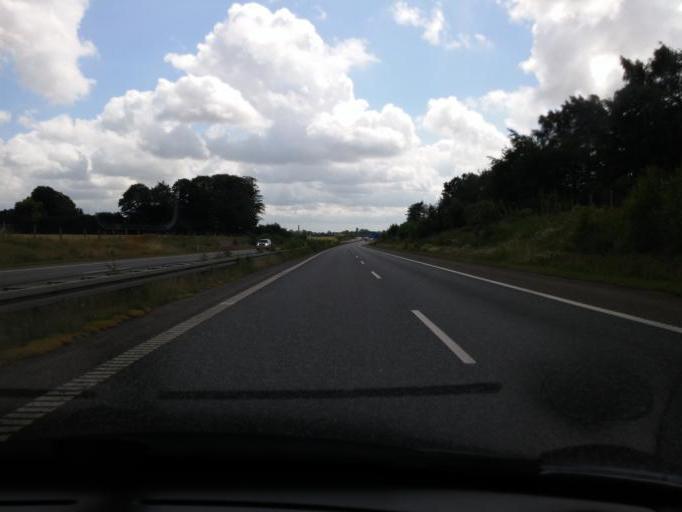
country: DK
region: South Denmark
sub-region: Faaborg-Midtfyn Kommune
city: Ringe
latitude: 55.2641
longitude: 10.4684
